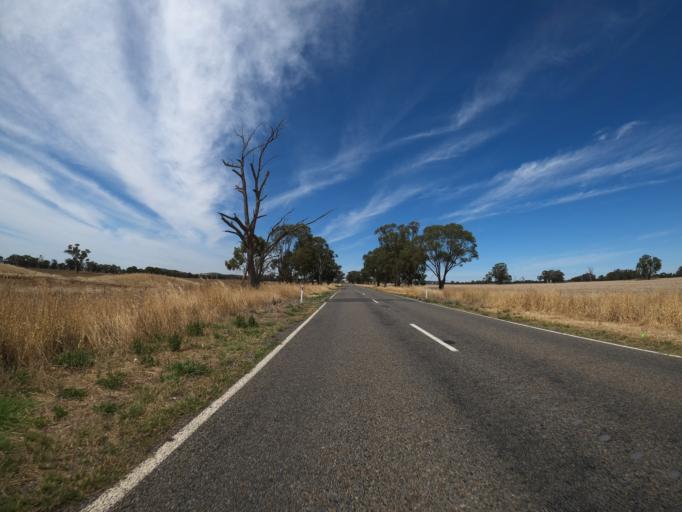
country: AU
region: Victoria
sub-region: Benalla
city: Benalla
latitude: -36.2949
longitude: 145.9523
